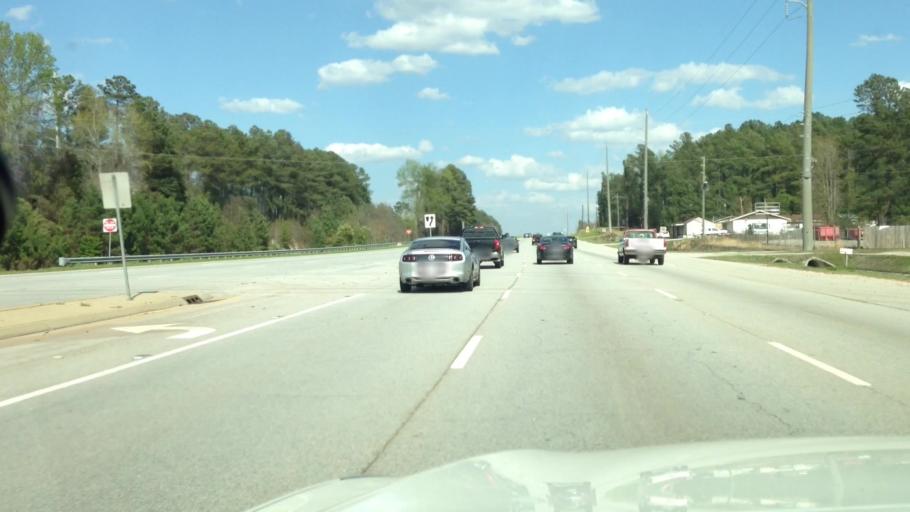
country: US
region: Georgia
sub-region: Columbia County
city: Martinez
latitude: 33.4439
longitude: -82.0967
